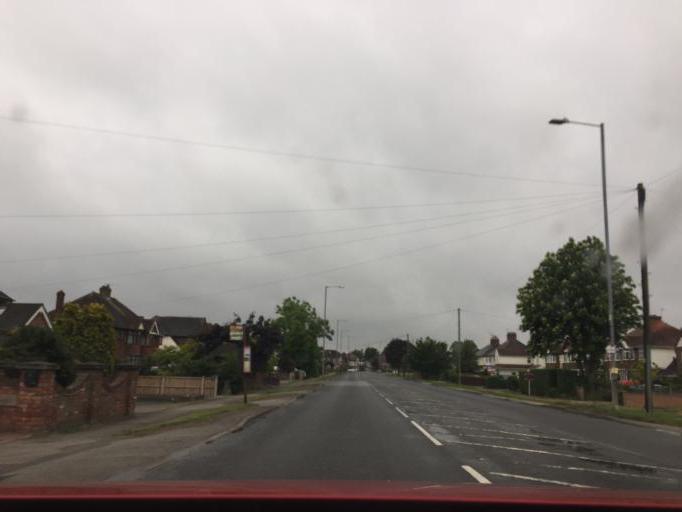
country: GB
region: England
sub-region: Warwickshire
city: Attleborough
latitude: 52.5325
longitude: -1.4251
